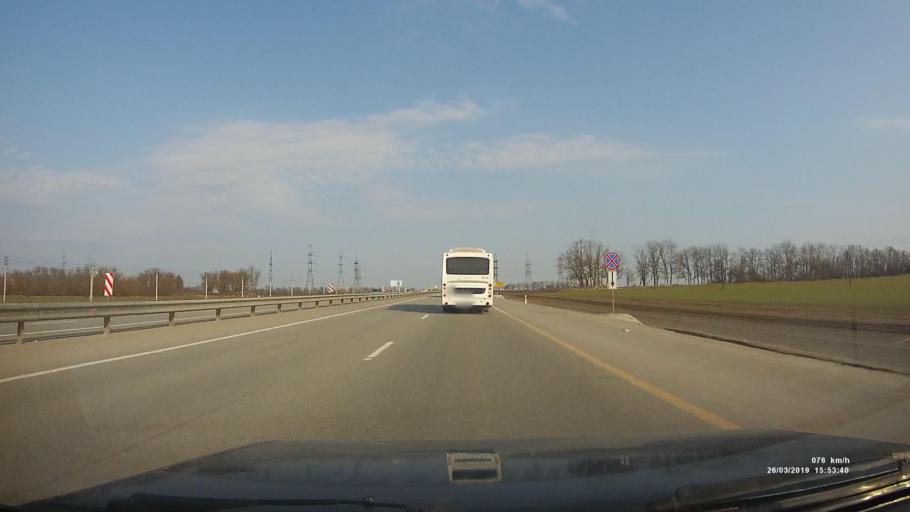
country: RU
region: Rostov
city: Krym
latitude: 47.2720
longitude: 39.5445
